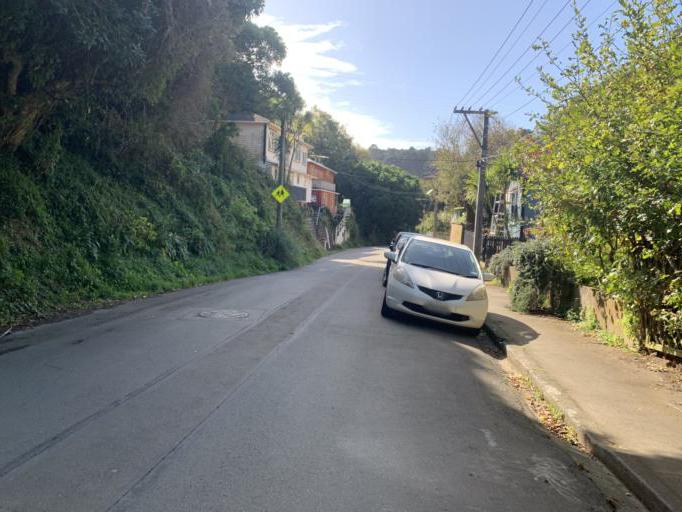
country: NZ
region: Wellington
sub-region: Wellington City
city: Kelburn
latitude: -41.2962
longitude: 174.7572
